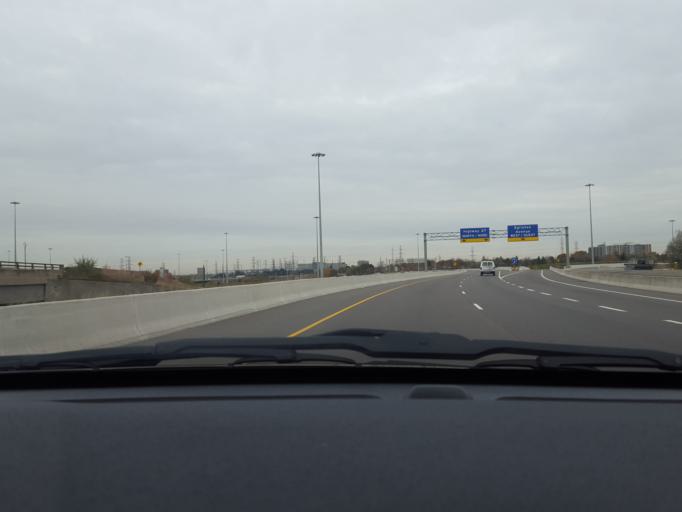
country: CA
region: Ontario
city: Etobicoke
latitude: 43.6689
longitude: -79.5735
